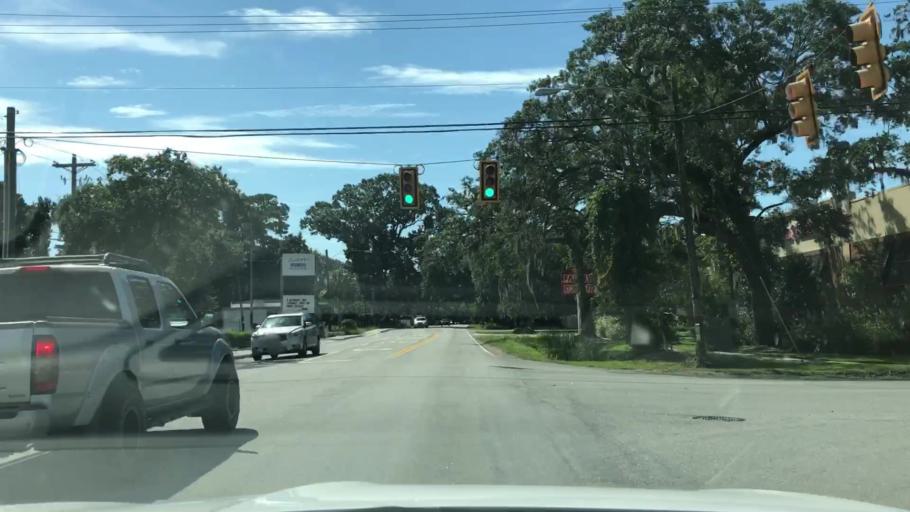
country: US
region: South Carolina
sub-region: Charleston County
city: North Charleston
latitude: 32.8256
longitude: -80.0393
